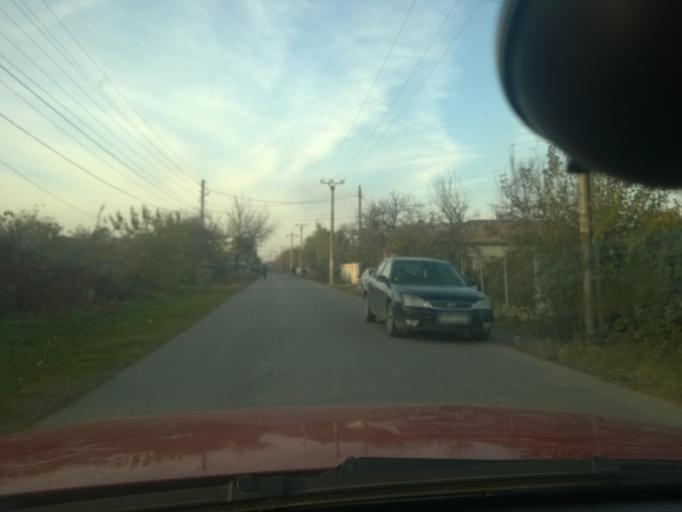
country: RO
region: Giurgiu
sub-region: Comuna Herasti
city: Herasti
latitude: 44.2114
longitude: 26.3607
